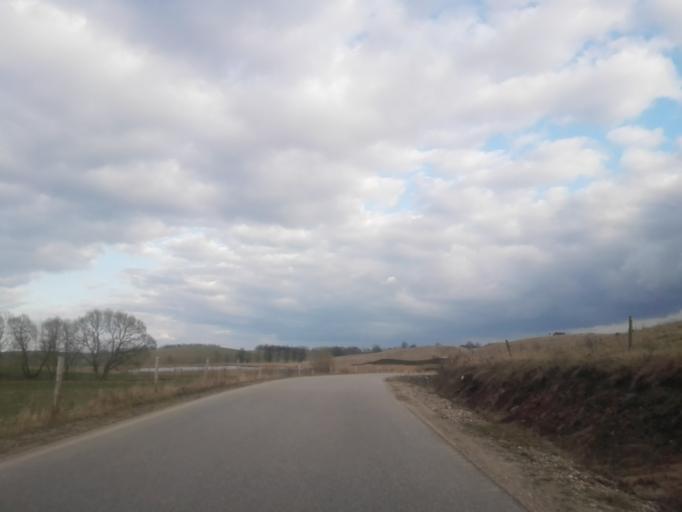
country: PL
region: Podlasie
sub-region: Suwalki
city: Suwalki
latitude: 54.2023
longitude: 22.9875
